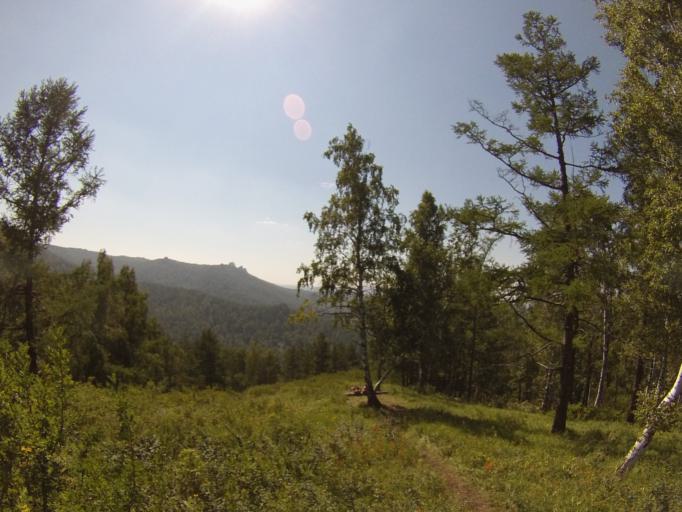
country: RU
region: Krasnoyarskiy
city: Krasnoyarsk
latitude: 55.9335
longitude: 92.7564
